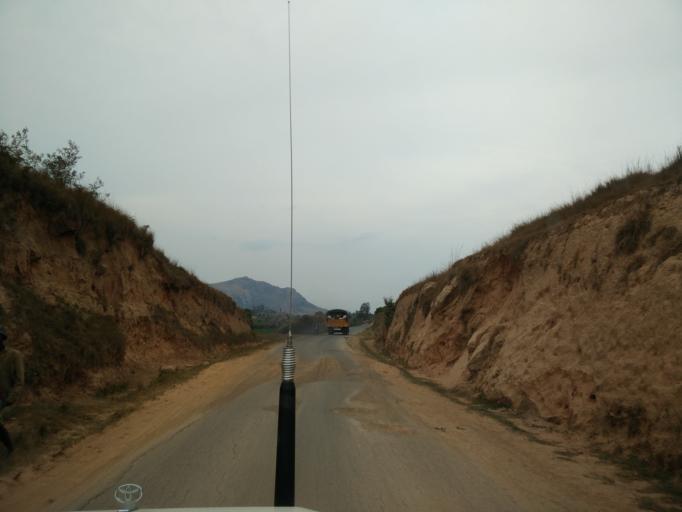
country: MG
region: Upper Matsiatra
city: Ambalavao
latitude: -21.6916
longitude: 46.9726
